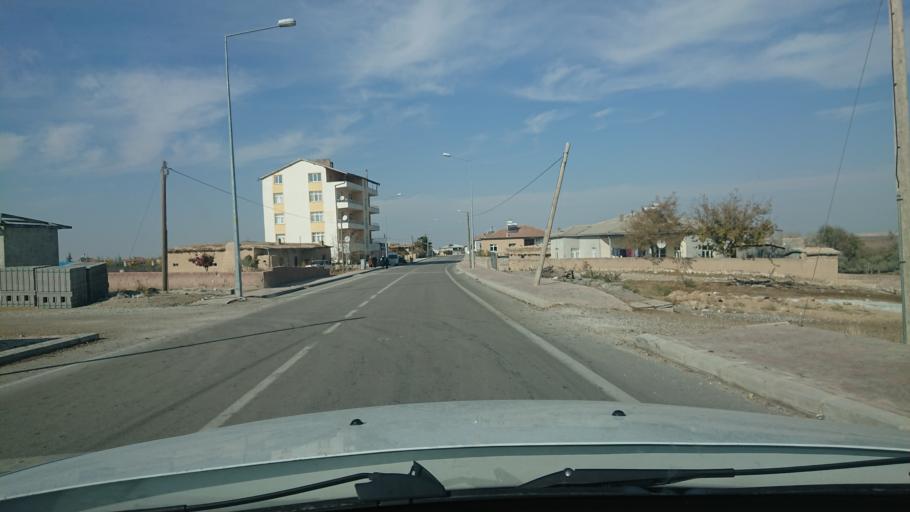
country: TR
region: Aksaray
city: Sultanhani
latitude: 38.2625
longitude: 33.4434
